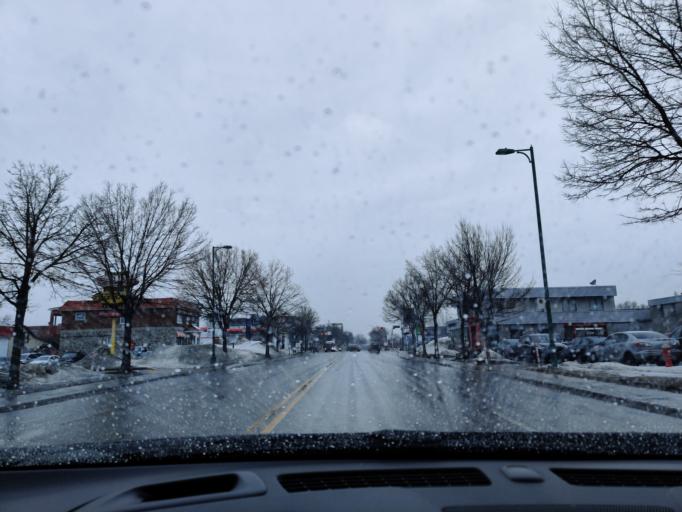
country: CA
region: Quebec
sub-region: Laval
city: Laval
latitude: 45.5481
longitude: -73.7561
